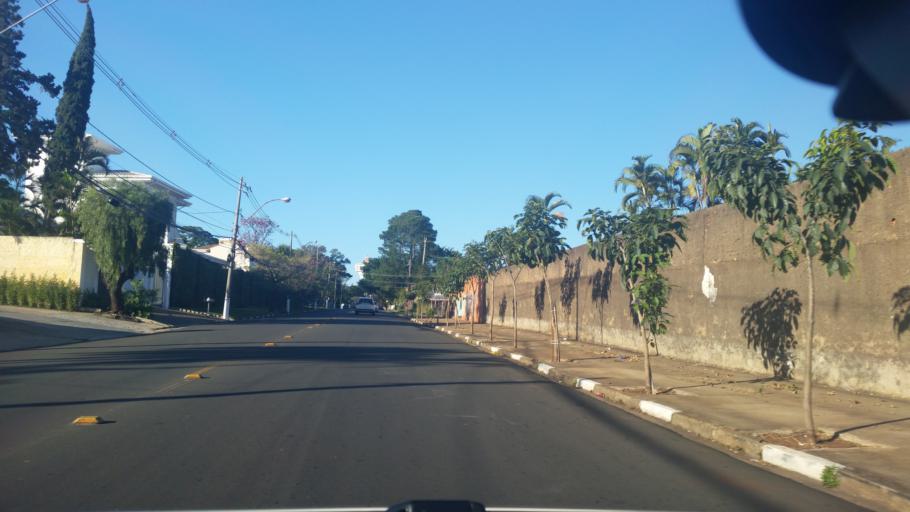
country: BR
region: Sao Paulo
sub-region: Campinas
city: Campinas
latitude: -22.8682
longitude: -47.0572
